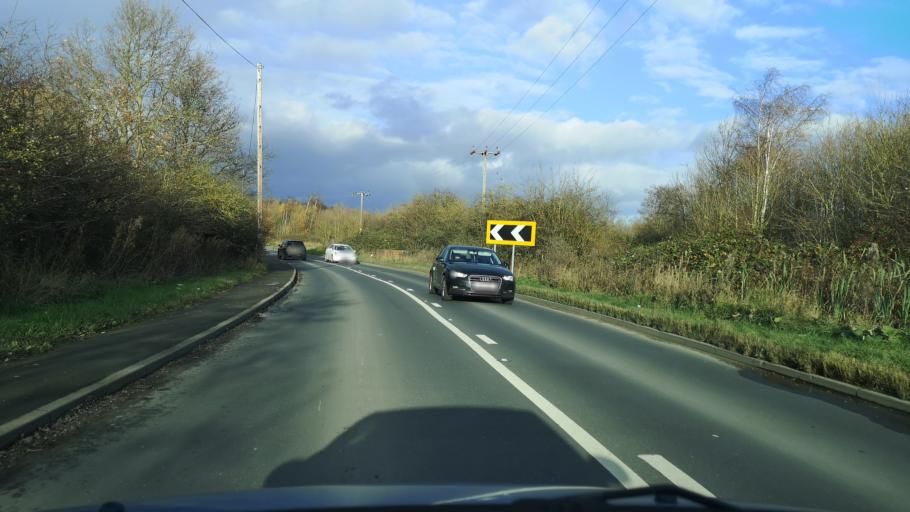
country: GB
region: England
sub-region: City and Borough of Wakefield
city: Featherstone
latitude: 53.6863
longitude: -1.3755
